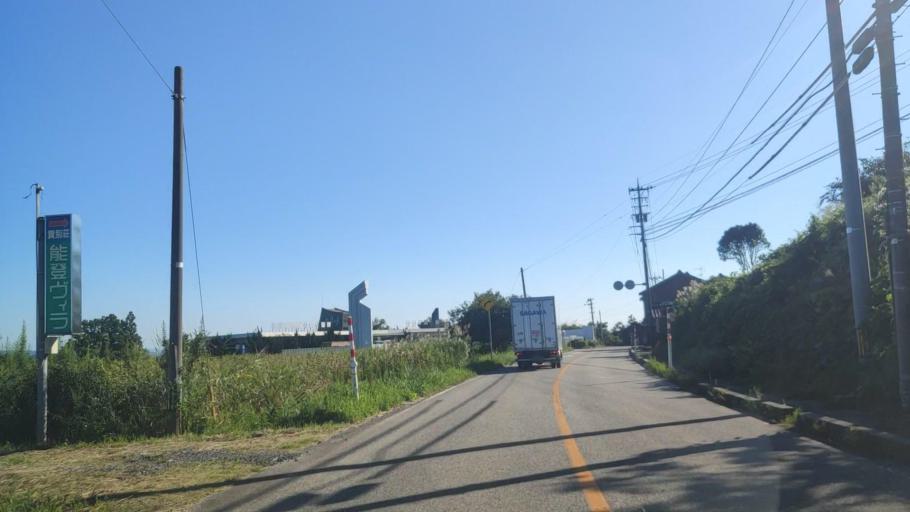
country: JP
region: Ishikawa
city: Nanao
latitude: 37.1941
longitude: 136.9109
